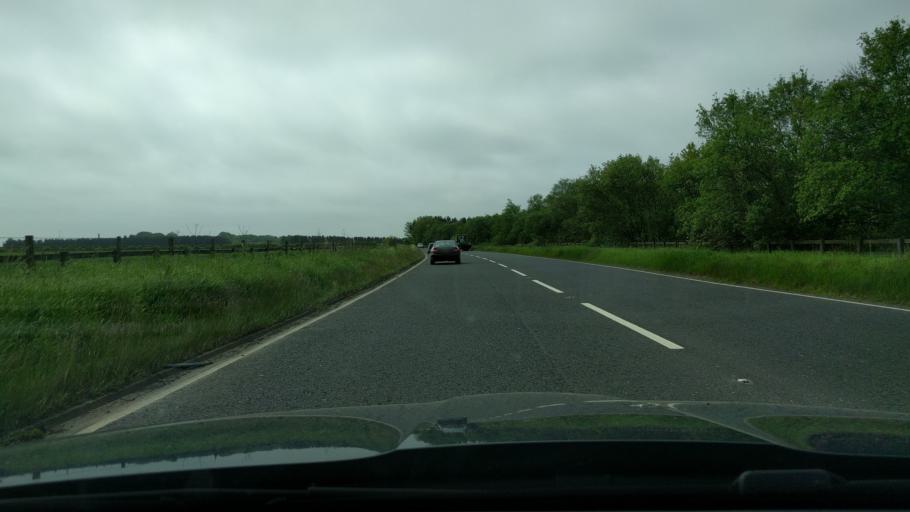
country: GB
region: England
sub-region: Northumberland
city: East Chevington
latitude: 55.2666
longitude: -1.6058
